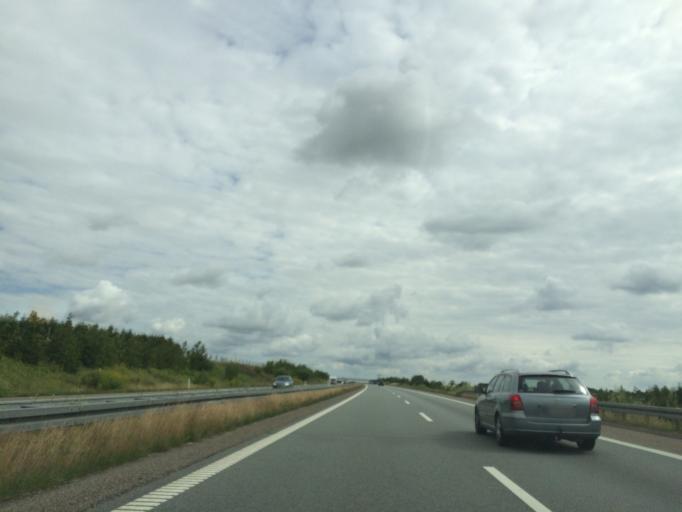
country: DK
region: Central Jutland
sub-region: Arhus Kommune
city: Hjortshoj
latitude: 56.2423
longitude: 10.2889
